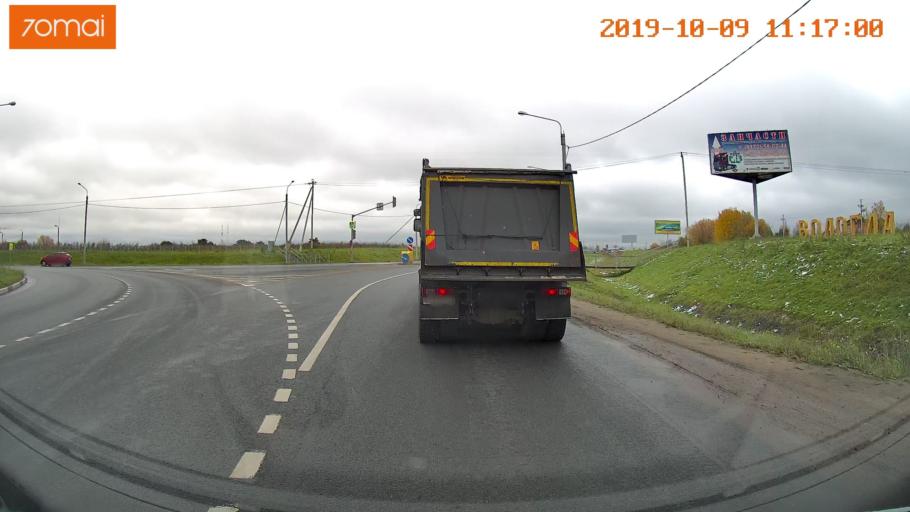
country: RU
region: Vologda
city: Vologda
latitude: 59.1758
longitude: 39.8933
